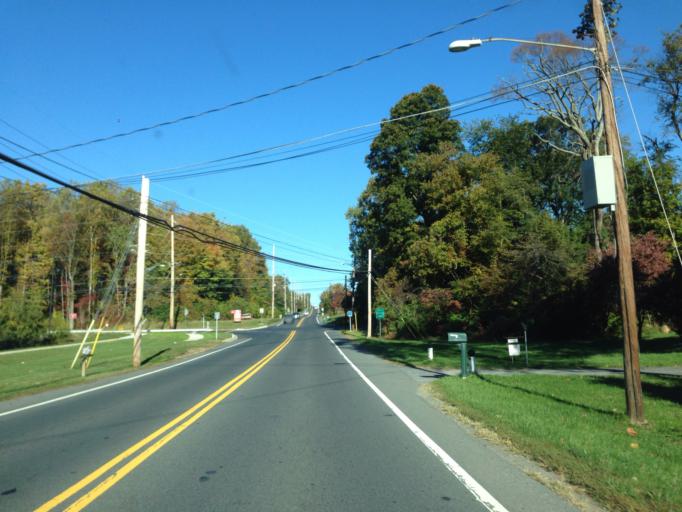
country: US
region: Maryland
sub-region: Montgomery County
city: Clarksburg
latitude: 39.2295
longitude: -77.2677
